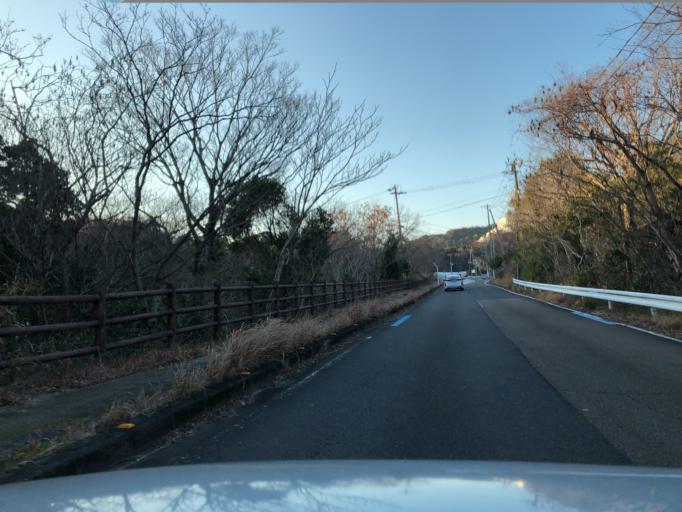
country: JP
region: Wakayama
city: Tanabe
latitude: 33.6615
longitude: 135.3757
